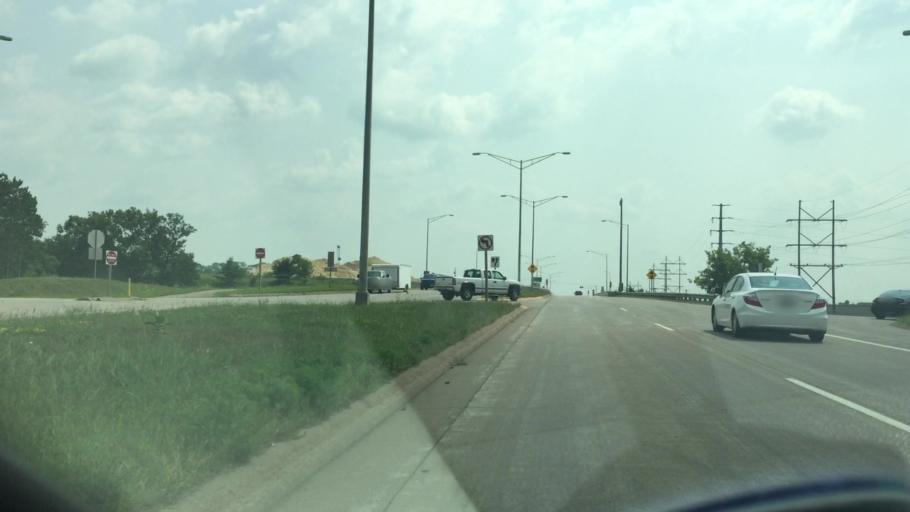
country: US
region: Wisconsin
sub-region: Eau Claire County
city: Altoona
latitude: 44.7674
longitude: -91.4592
